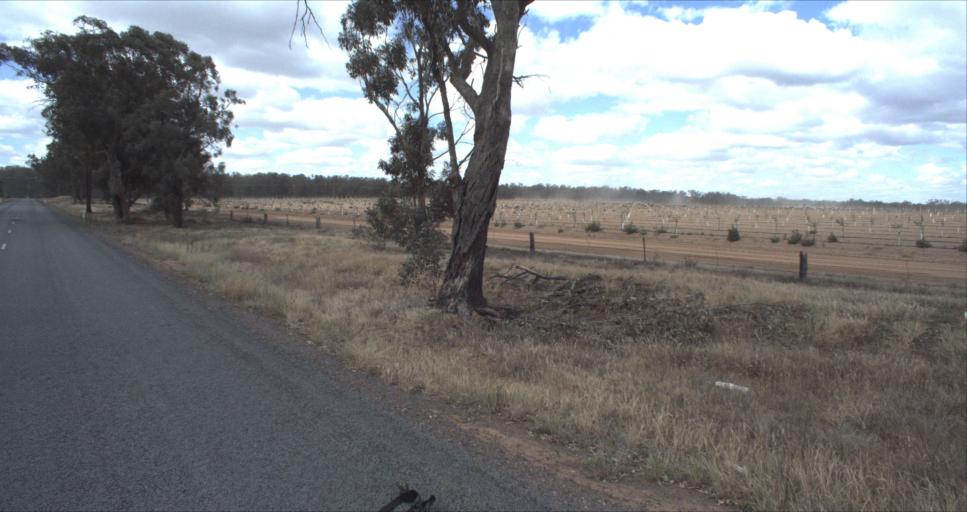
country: AU
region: New South Wales
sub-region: Leeton
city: Leeton
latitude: -34.6473
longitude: 146.3519
